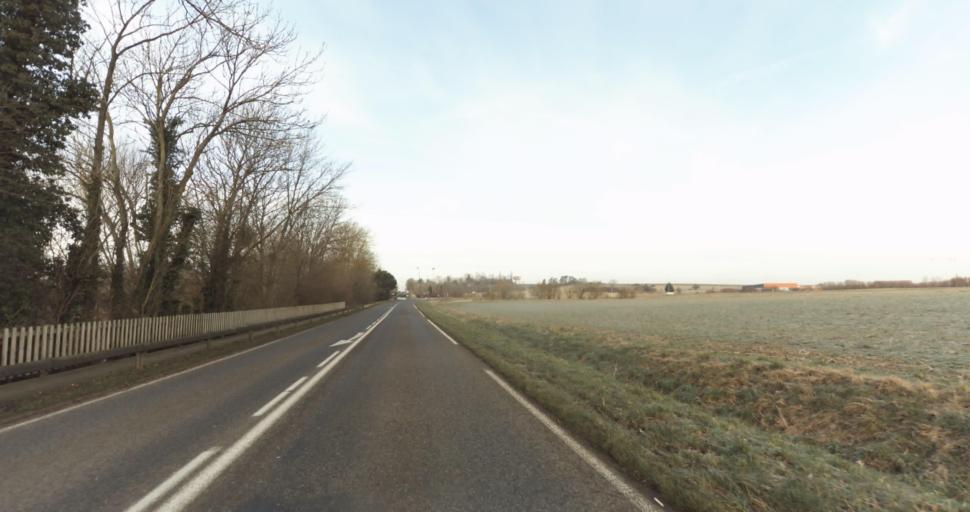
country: FR
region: Lorraine
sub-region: Departement de Meurthe-et-Moselle
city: Giraumont
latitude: 49.1510
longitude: 5.9055
